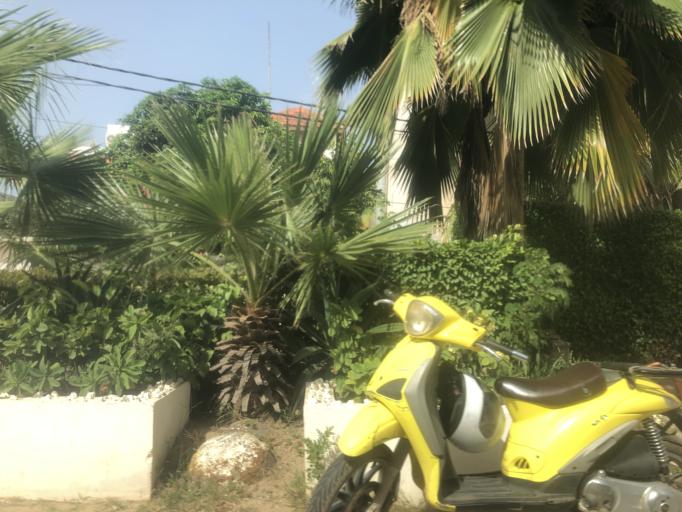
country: SN
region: Dakar
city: Mermoz Boabab
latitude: 14.7397
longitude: -17.5152
